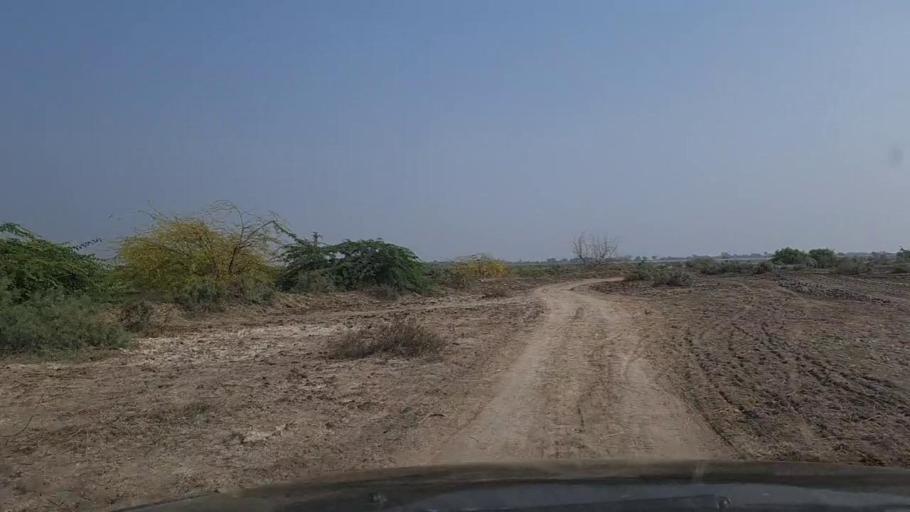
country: PK
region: Sindh
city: Mirpur Batoro
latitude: 24.6777
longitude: 68.2437
